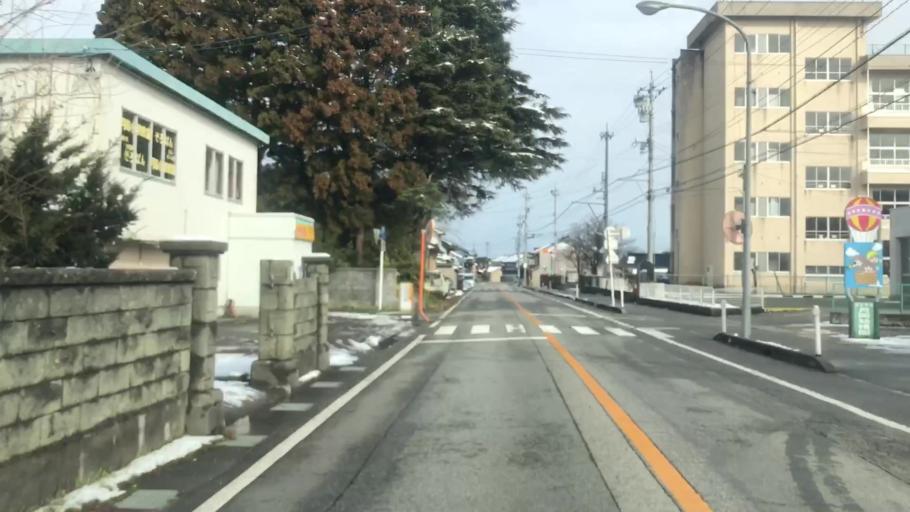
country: JP
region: Toyama
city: Toyama-shi
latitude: 36.6221
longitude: 137.2522
